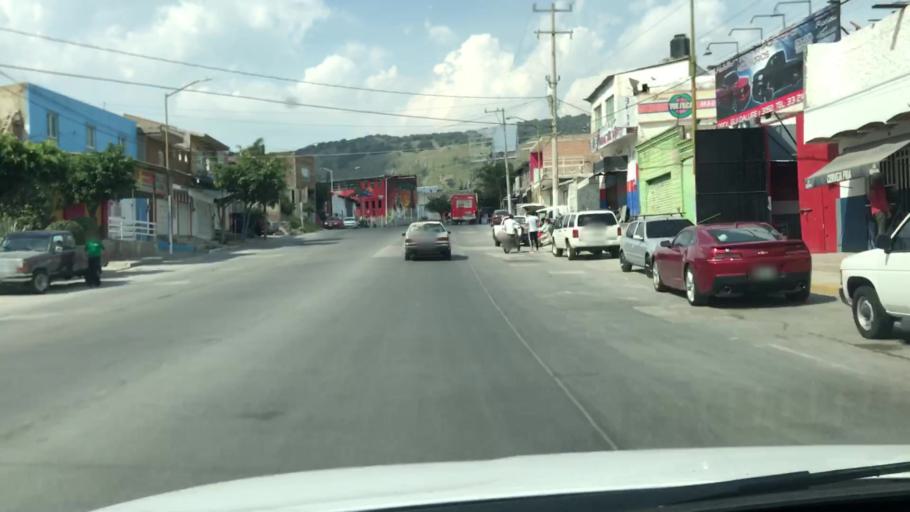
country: MX
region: Jalisco
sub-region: Tlajomulco de Zuniga
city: Palomar
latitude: 20.6393
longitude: -103.4608
